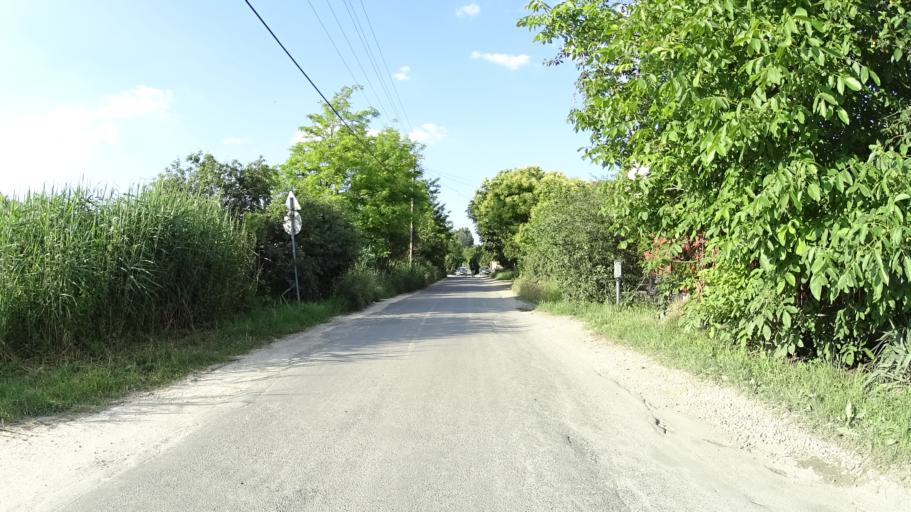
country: HU
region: Budapest
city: Budapest XXIII. keruelet
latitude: 47.3806
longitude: 19.0957
